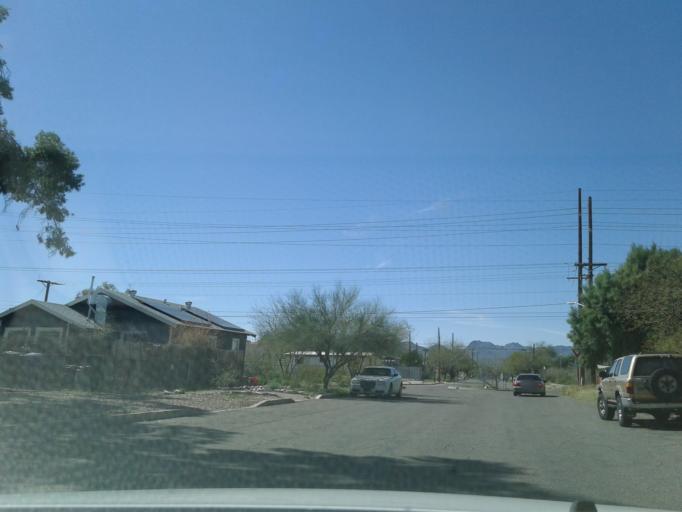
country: US
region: Arizona
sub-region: Pima County
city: South Tucson
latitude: 32.2342
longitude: -110.9757
